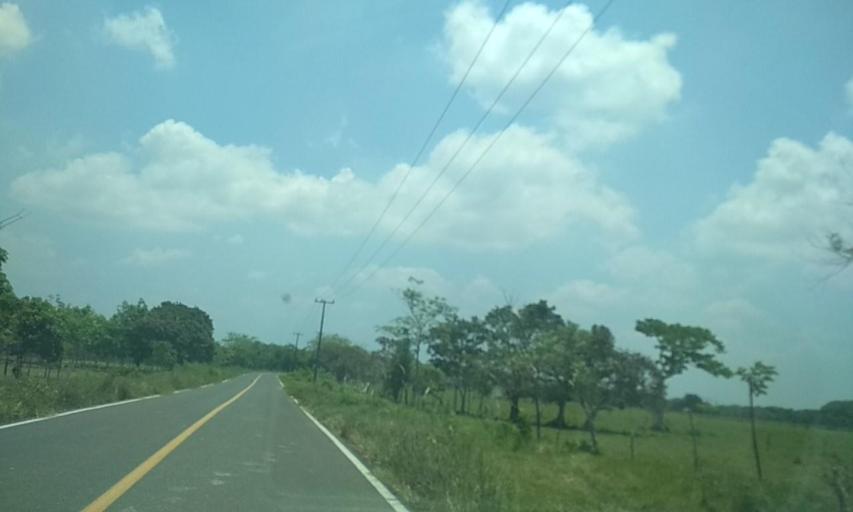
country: MX
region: Tabasco
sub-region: Huimanguillo
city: Francisco Rueda
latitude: 17.7578
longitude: -94.0531
